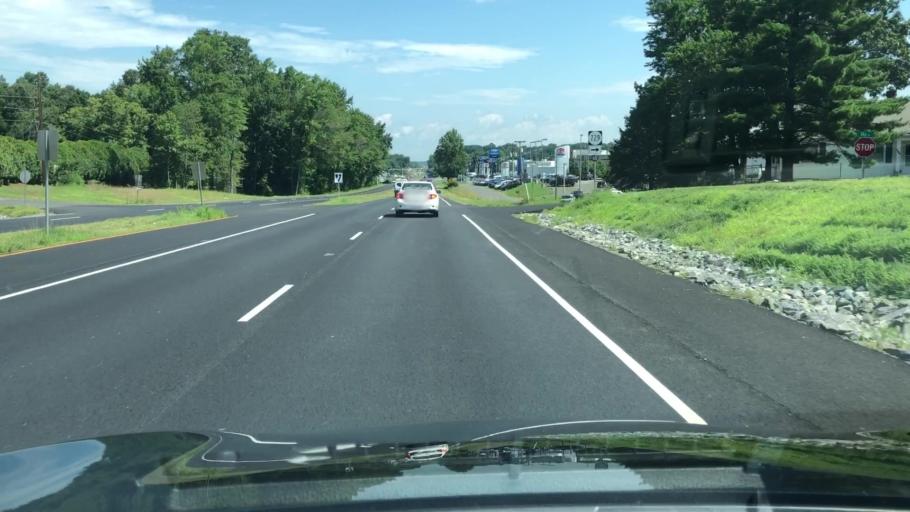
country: US
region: Virginia
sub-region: City of Fredericksburg
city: Fredericksburg
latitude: 38.2679
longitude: -77.4940
